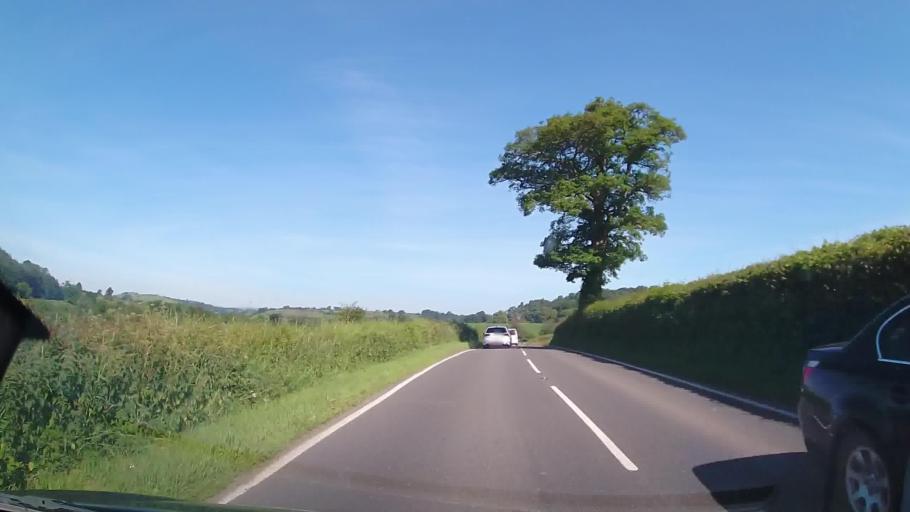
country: GB
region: Wales
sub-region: Sir Powys
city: Llanfyllin
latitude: 52.6577
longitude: -3.2605
